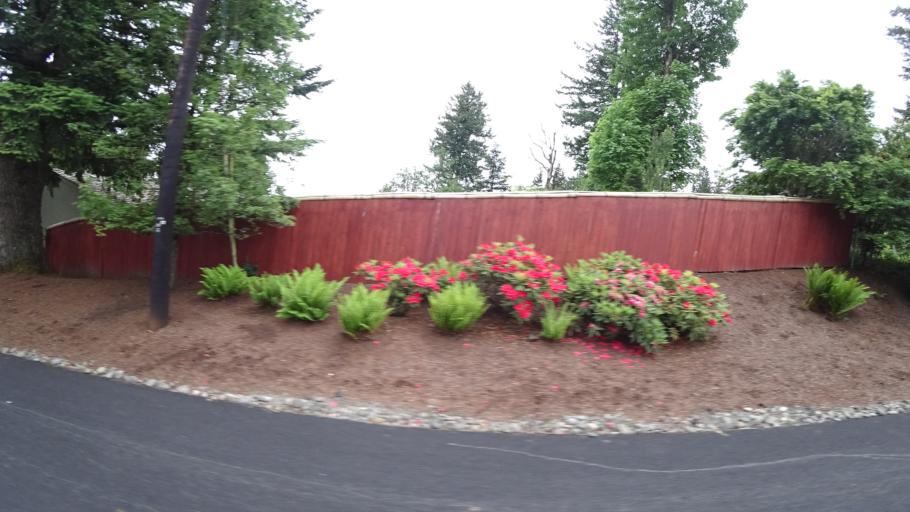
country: US
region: Oregon
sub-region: Multnomah County
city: Portland
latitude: 45.4860
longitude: -122.6915
